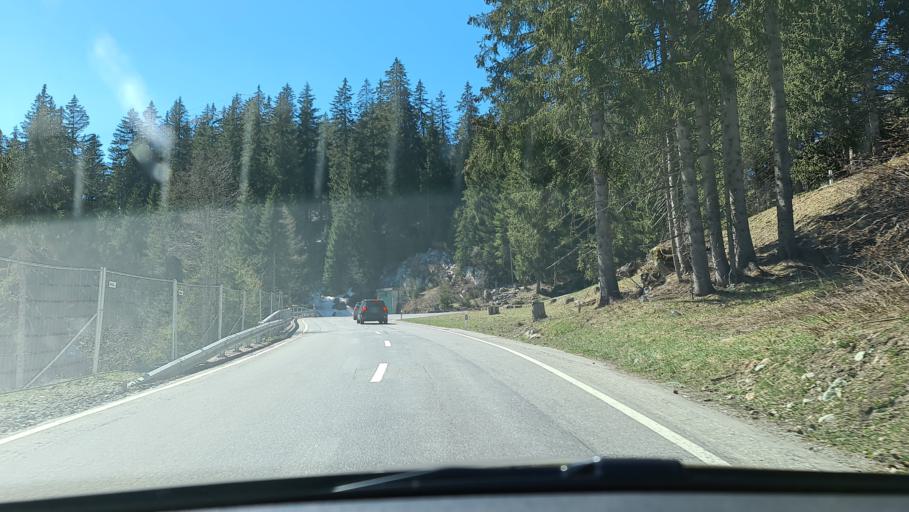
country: CH
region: Grisons
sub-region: Hinterrhein District
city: Thusis
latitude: 46.5689
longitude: 9.3848
